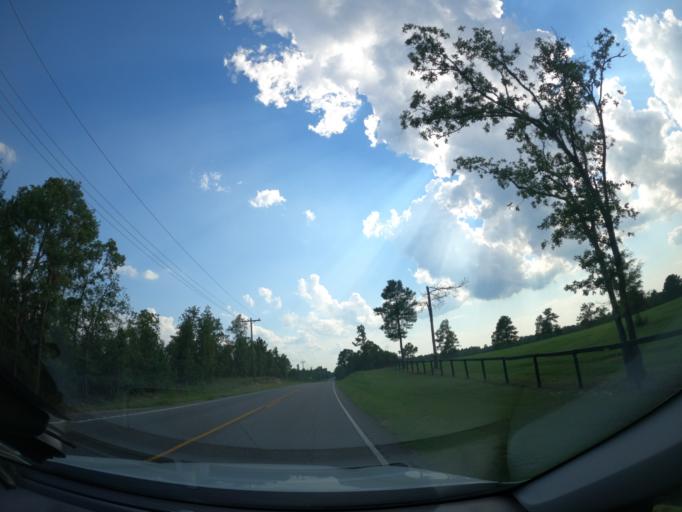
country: US
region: South Carolina
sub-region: Barnwell County
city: Williston
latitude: 33.5075
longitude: -81.5058
